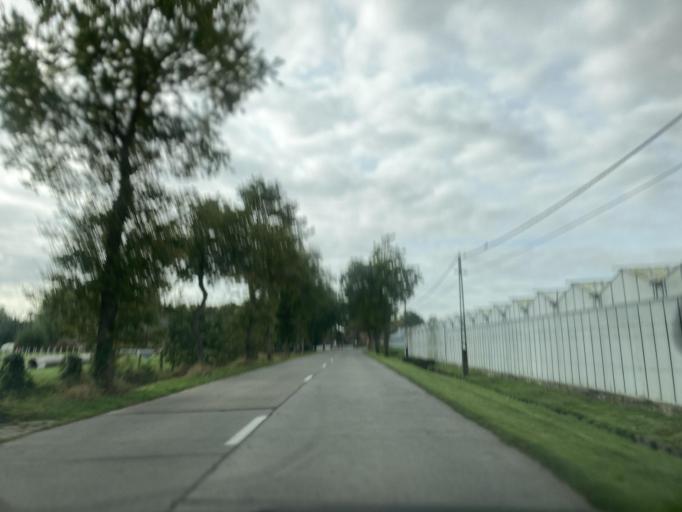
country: BE
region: Flanders
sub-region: Provincie West-Vlaanderen
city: Lichtervelde
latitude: 51.0521
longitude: 3.1790
